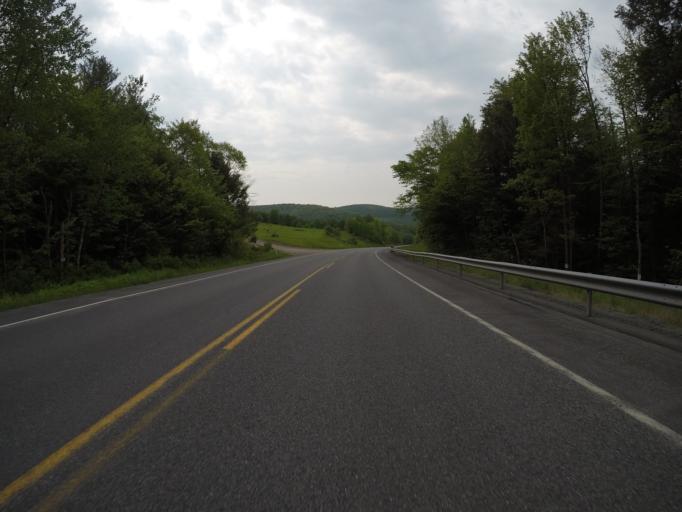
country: US
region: New York
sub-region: Sullivan County
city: Livingston Manor
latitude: 42.0300
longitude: -74.8959
